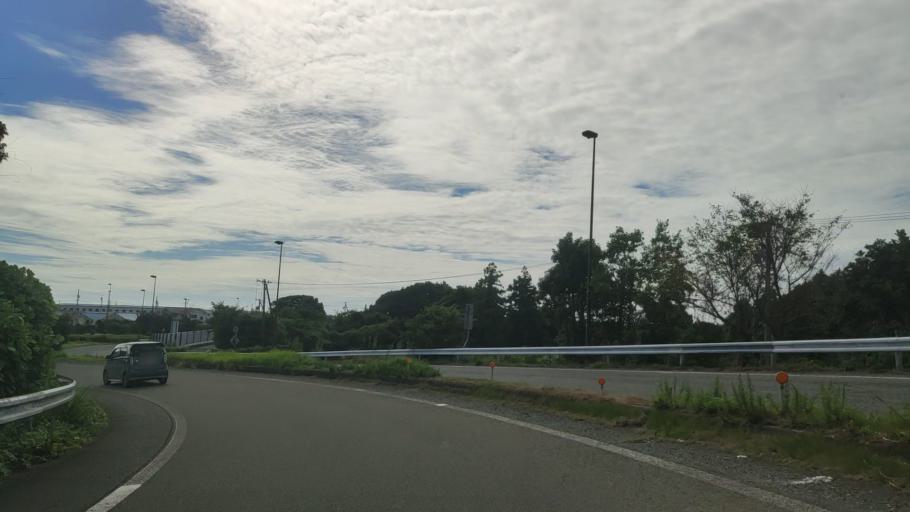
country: JP
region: Shizuoka
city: Hamamatsu
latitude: 34.7660
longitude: 137.6784
